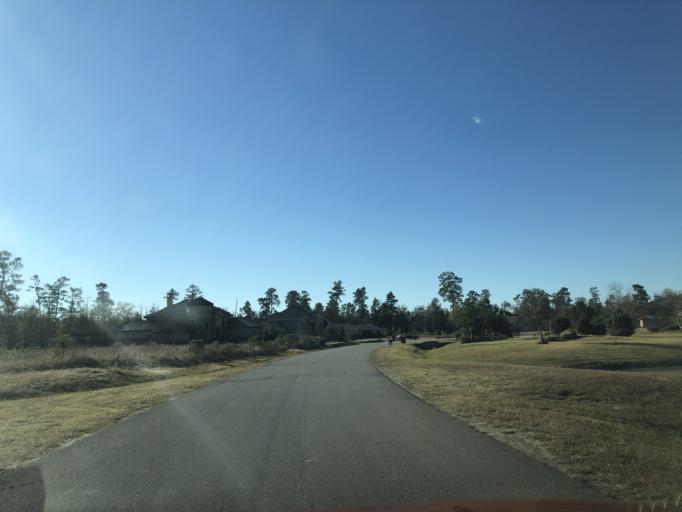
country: US
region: Texas
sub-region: Montgomery County
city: Porter Heights
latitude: 30.0732
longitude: -95.3183
